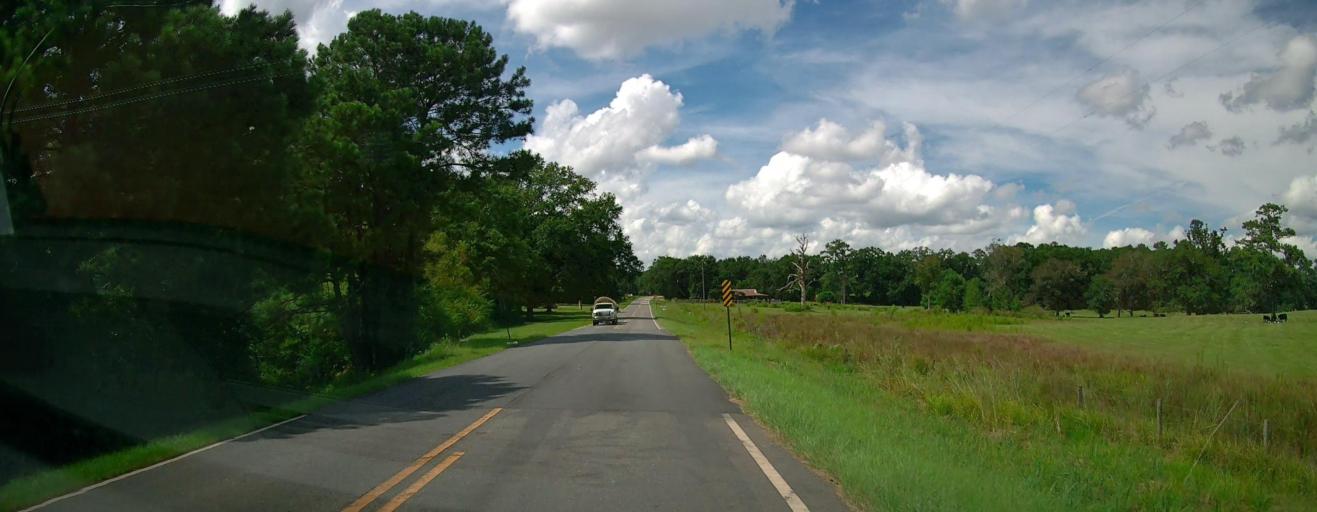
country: US
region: Georgia
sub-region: Taylor County
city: Butler
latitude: 32.5402
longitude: -84.2213
